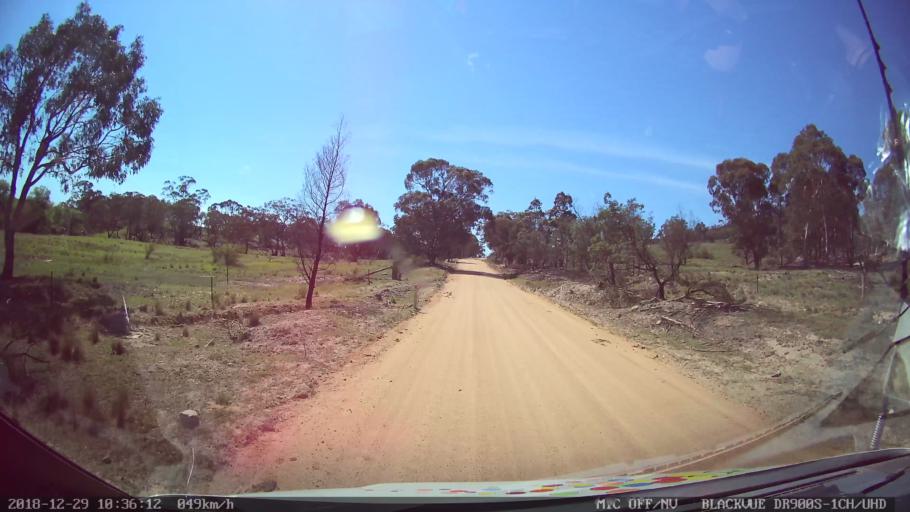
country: AU
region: New South Wales
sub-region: Yass Valley
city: Gundaroo
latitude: -34.9928
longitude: 149.4892
